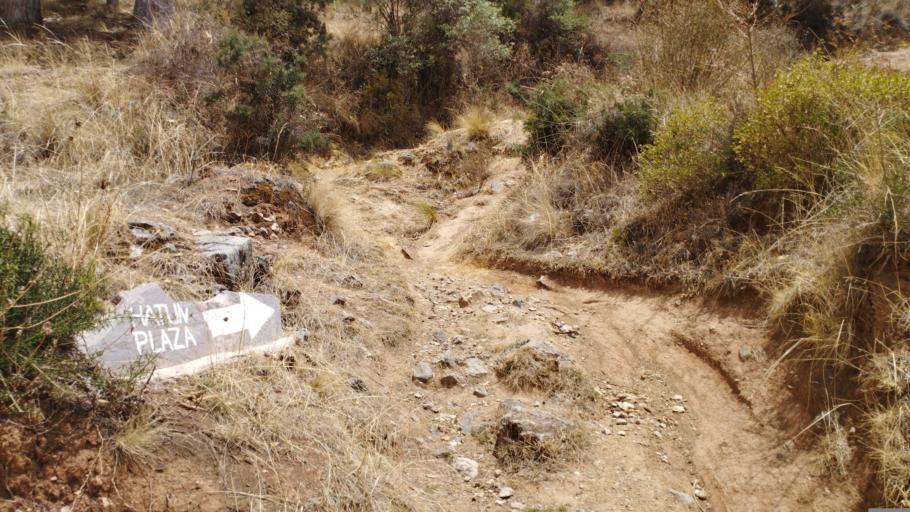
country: PE
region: Cusco
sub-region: Provincia de Cusco
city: Cusco
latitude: -13.5193
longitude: -71.9447
